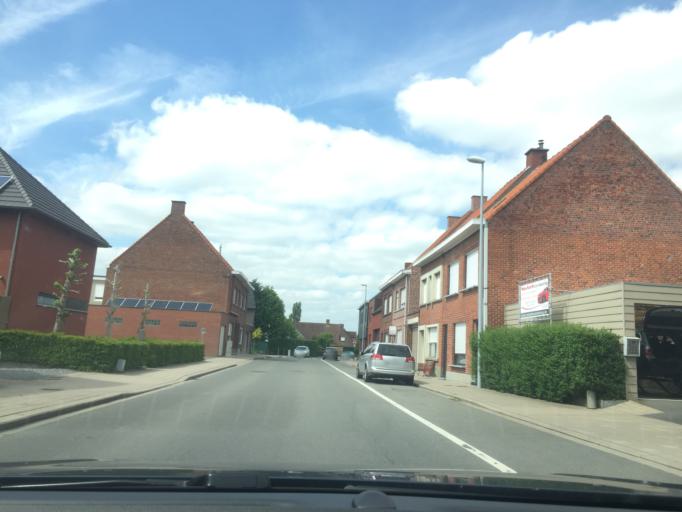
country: BE
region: Flanders
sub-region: Provincie West-Vlaanderen
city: Izegem
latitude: 50.9139
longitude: 3.2293
